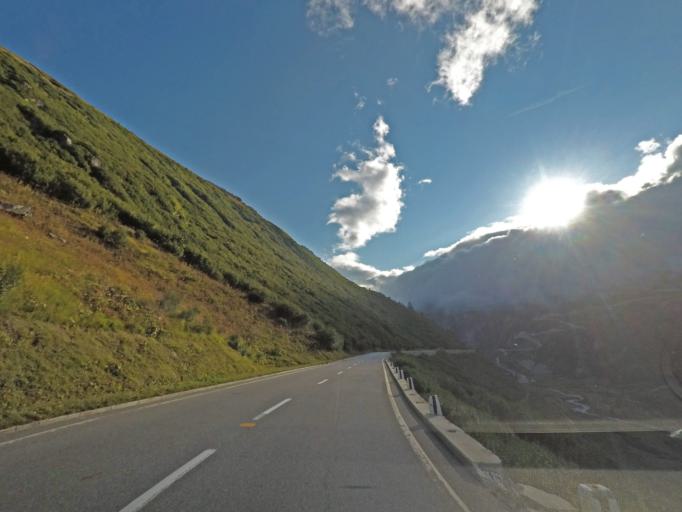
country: IT
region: Piedmont
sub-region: Provincia Verbano-Cusio-Ossola
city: Formazza
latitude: 46.5657
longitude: 8.3810
